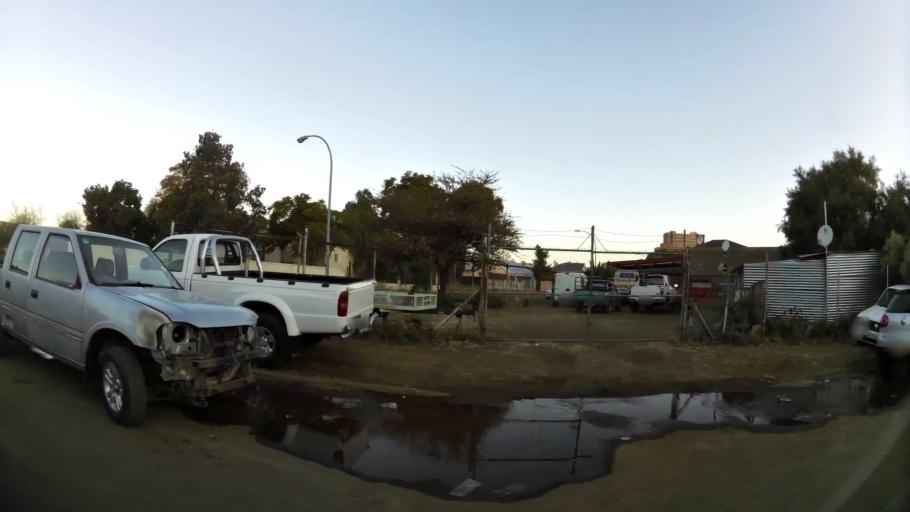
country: ZA
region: Northern Cape
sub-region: Frances Baard District Municipality
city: Kimberley
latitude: -28.7329
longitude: 24.7677
